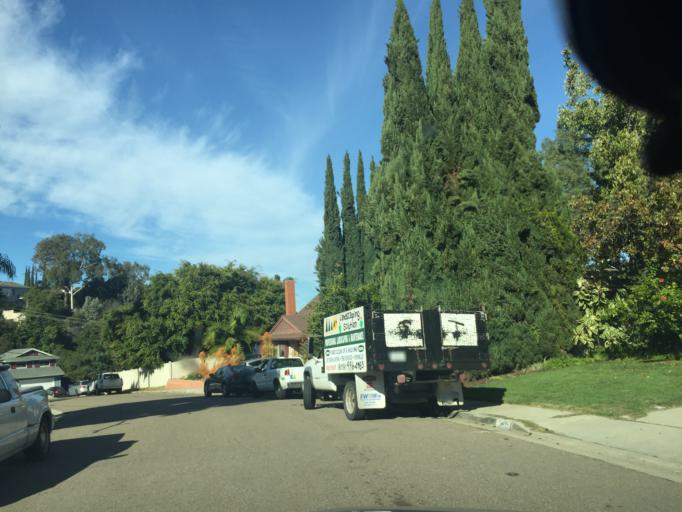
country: US
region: California
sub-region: San Diego County
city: Lemon Grove
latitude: 32.7651
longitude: -117.0787
